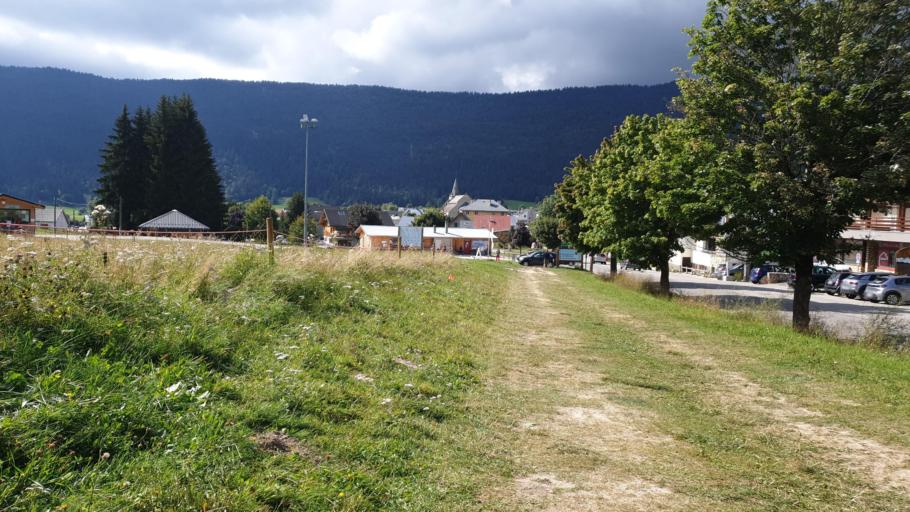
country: FR
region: Rhone-Alpes
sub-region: Departement de l'Isere
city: Autrans
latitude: 45.1728
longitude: 5.5464
